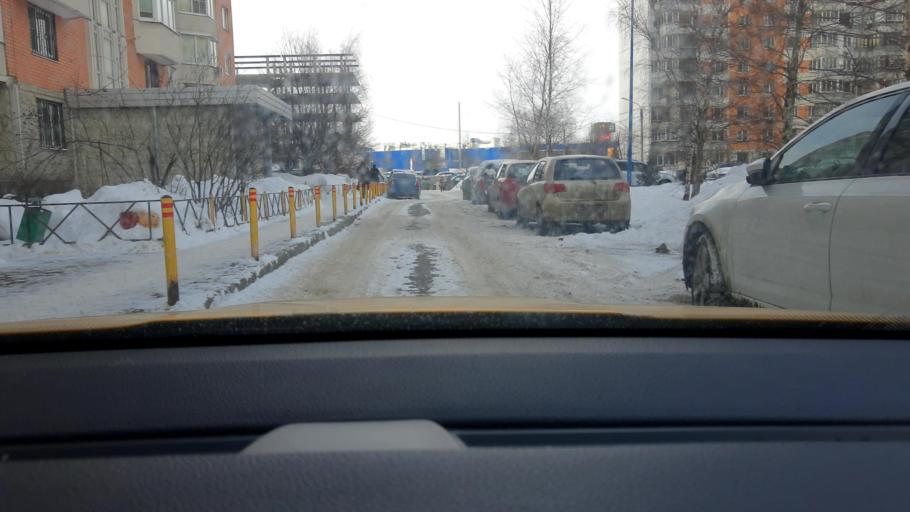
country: RU
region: Moscow
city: Khimki
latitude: 55.9079
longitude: 37.4034
